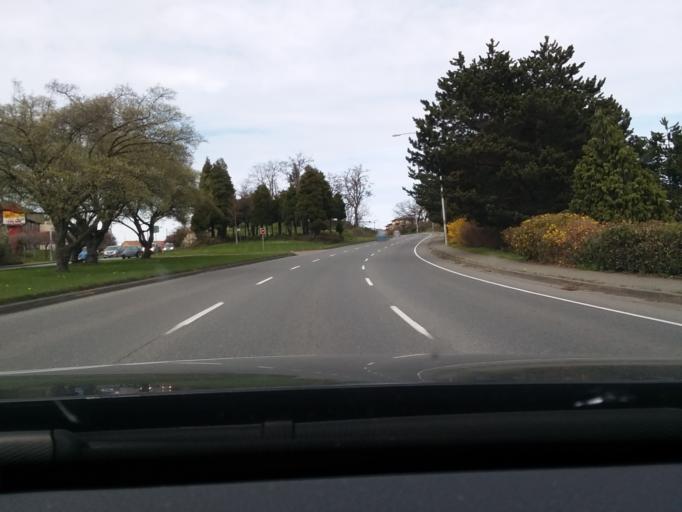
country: CA
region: British Columbia
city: Victoria
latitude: 48.4533
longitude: -123.3711
